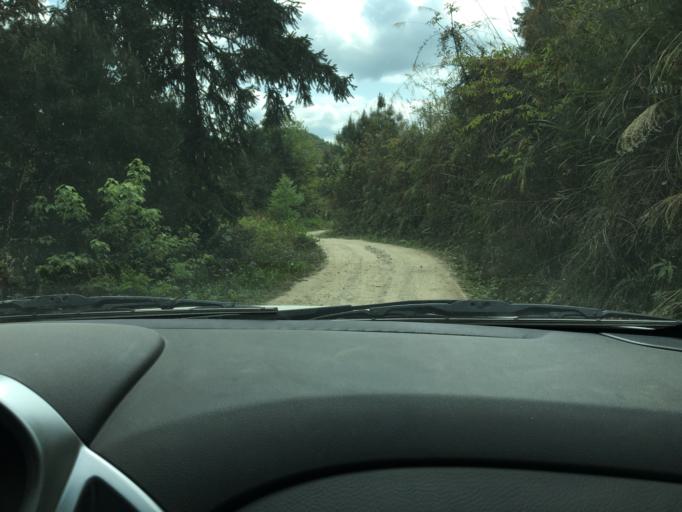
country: CN
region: Guizhou Sheng
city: Kuanping
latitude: 28.0262
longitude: 108.0521
